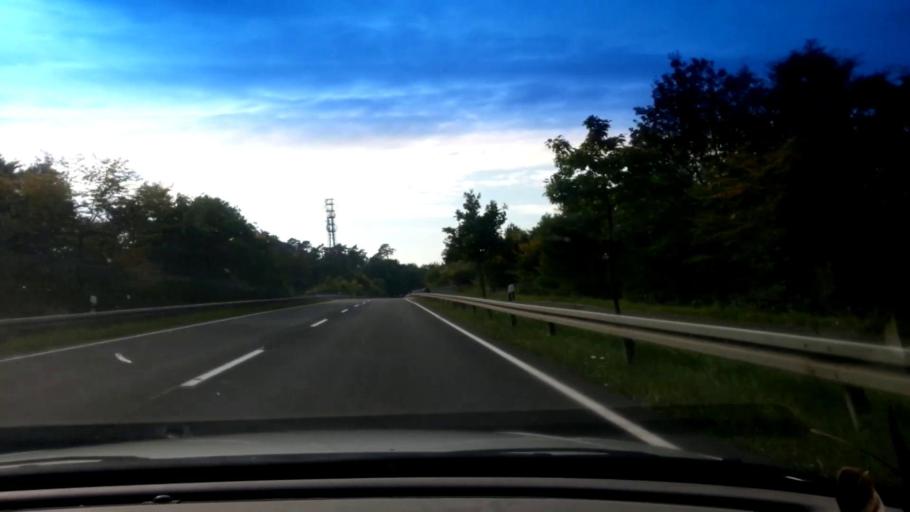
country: DE
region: Bavaria
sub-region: Upper Franconia
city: Memmelsdorf
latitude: 49.8888
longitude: 10.9510
